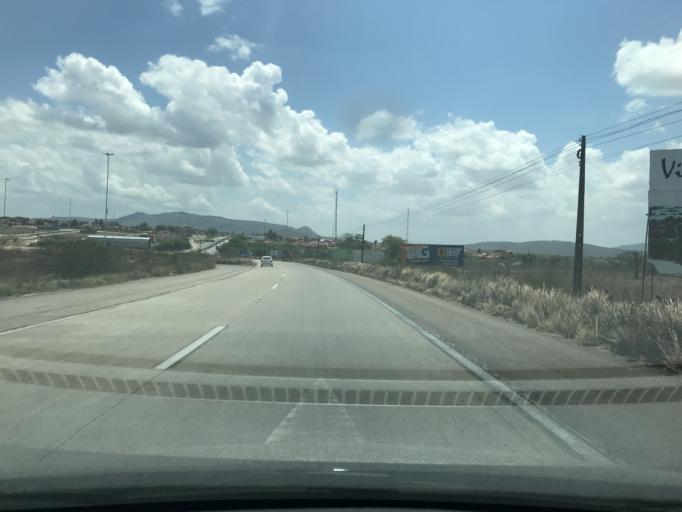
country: BR
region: Pernambuco
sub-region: Bezerros
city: Bezerros
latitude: -8.2981
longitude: -35.8366
